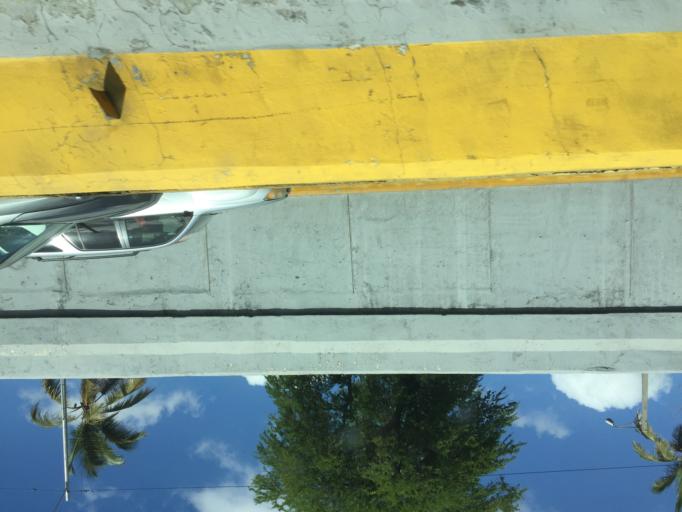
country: DO
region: Santo Domingo
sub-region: Santo Domingo
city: Santo Domingo Este
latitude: 18.4848
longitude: -69.8644
